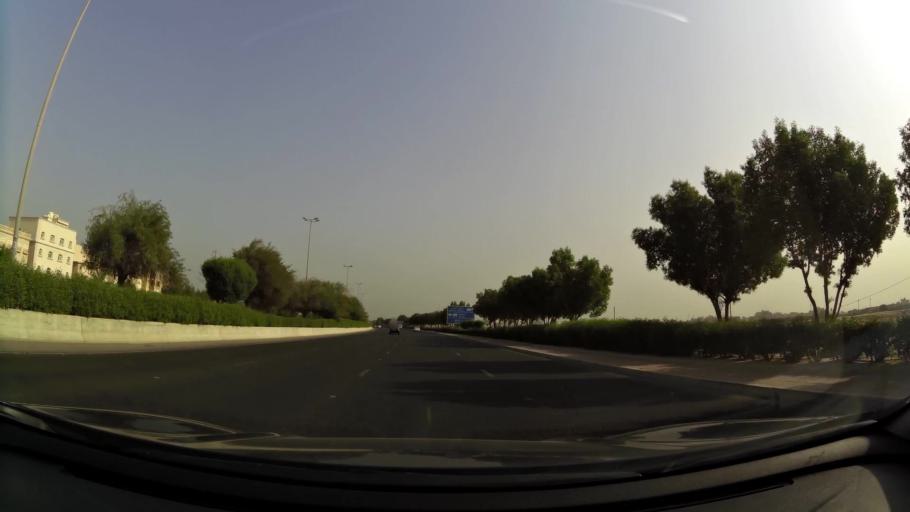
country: KW
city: Al Funaytis
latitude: 29.2286
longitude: 48.0768
